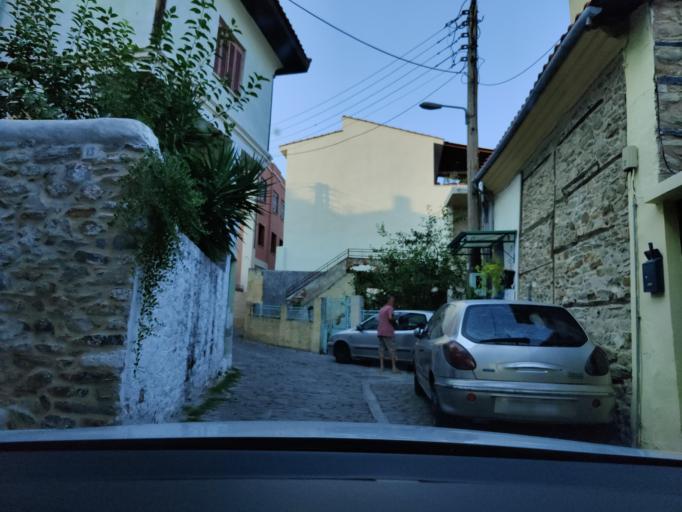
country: GR
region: East Macedonia and Thrace
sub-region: Nomos Kavalas
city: Kavala
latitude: 40.9332
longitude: 24.4155
